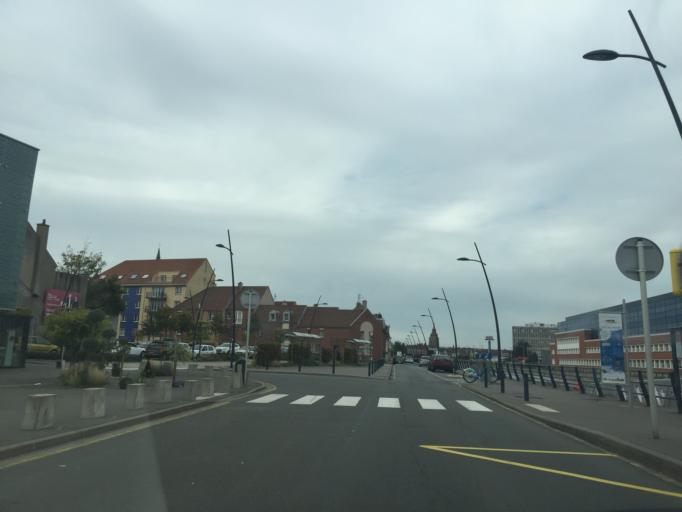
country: FR
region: Nord-Pas-de-Calais
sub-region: Departement du Pas-de-Calais
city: Calais
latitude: 50.9504
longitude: 1.8601
